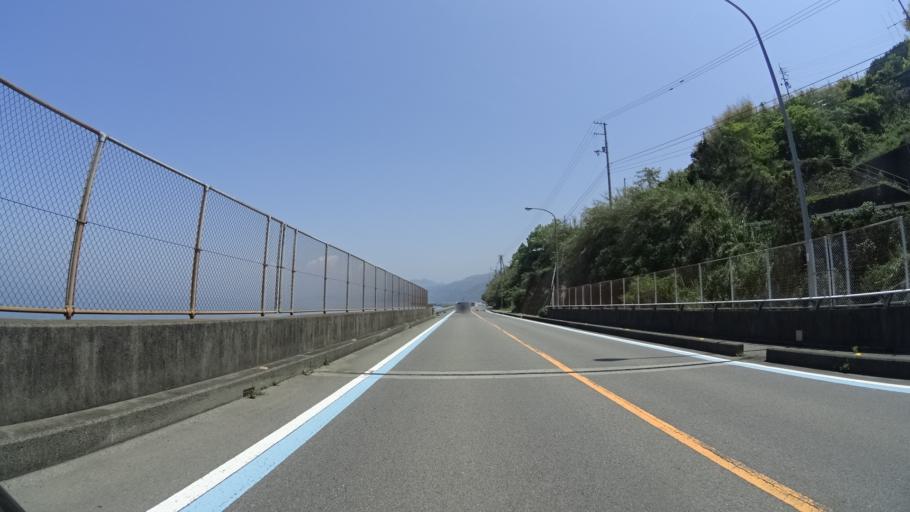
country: JP
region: Ehime
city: Ozu
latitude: 33.6470
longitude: 132.5615
